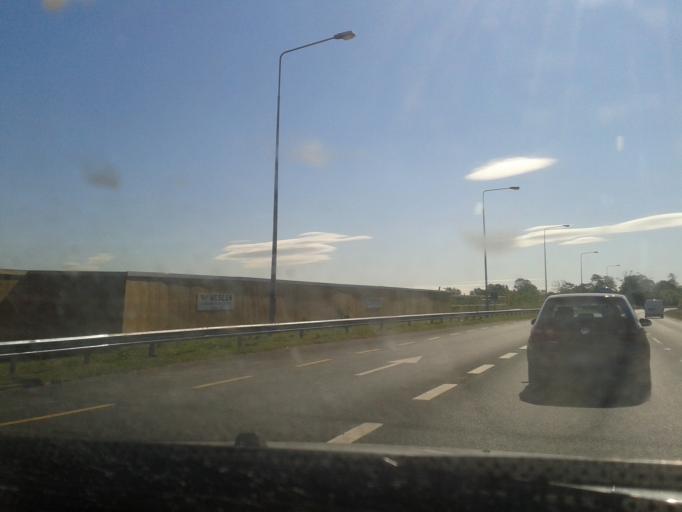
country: IE
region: Leinster
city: Hartstown
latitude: 53.4058
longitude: -6.4114
